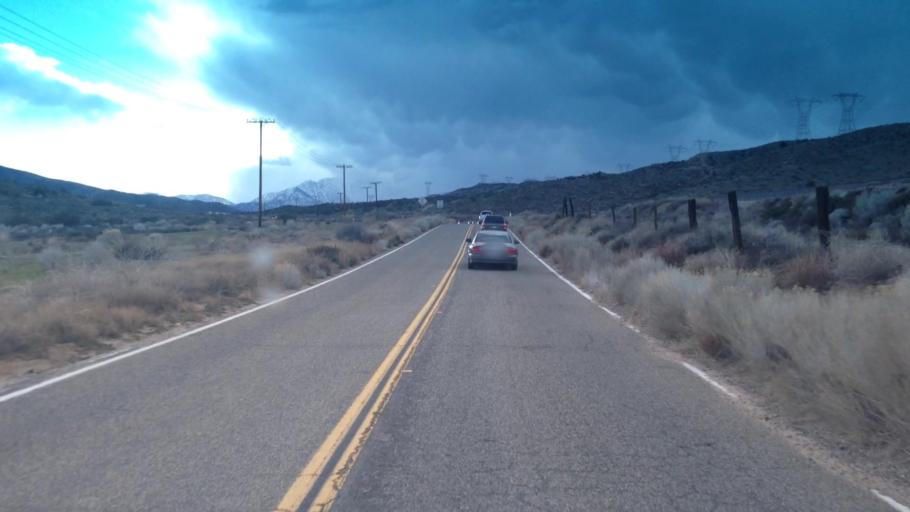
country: US
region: California
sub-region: San Bernardino County
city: Oak Hills
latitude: 34.3486
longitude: -117.3902
